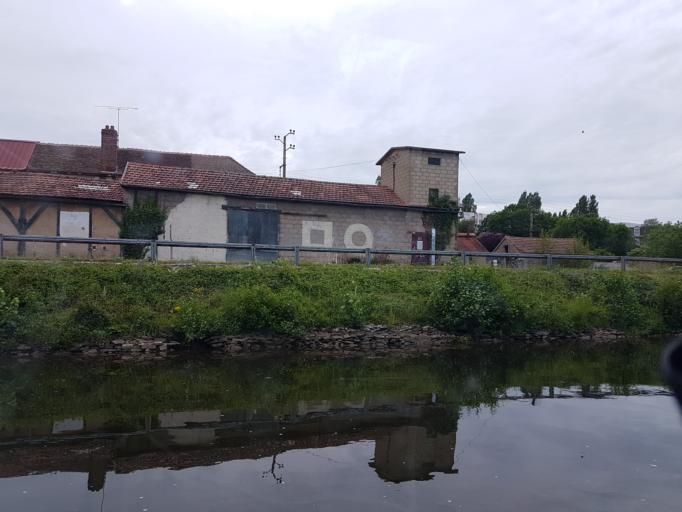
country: FR
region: Bourgogne
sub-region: Departement de l'Yonne
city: Auxerre
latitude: 47.8059
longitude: 3.5755
